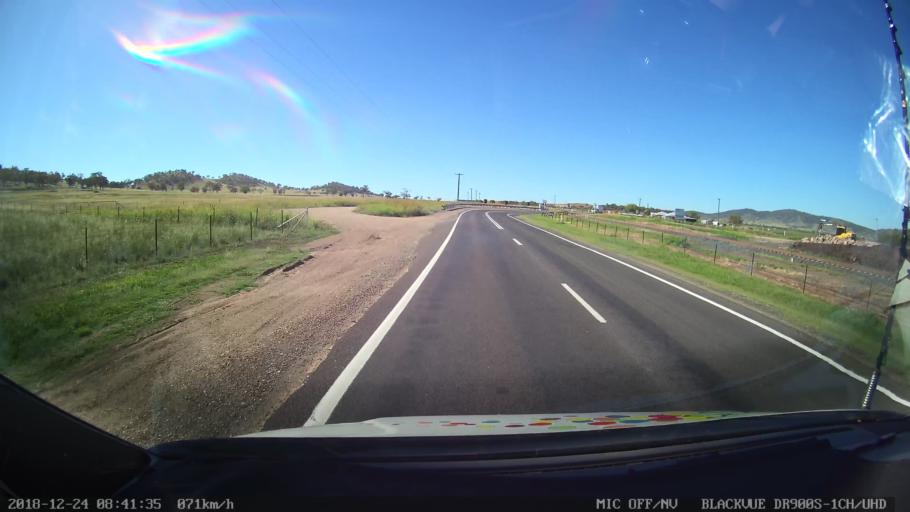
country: AU
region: New South Wales
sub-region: Liverpool Plains
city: Quirindi
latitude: -31.3647
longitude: 150.6450
